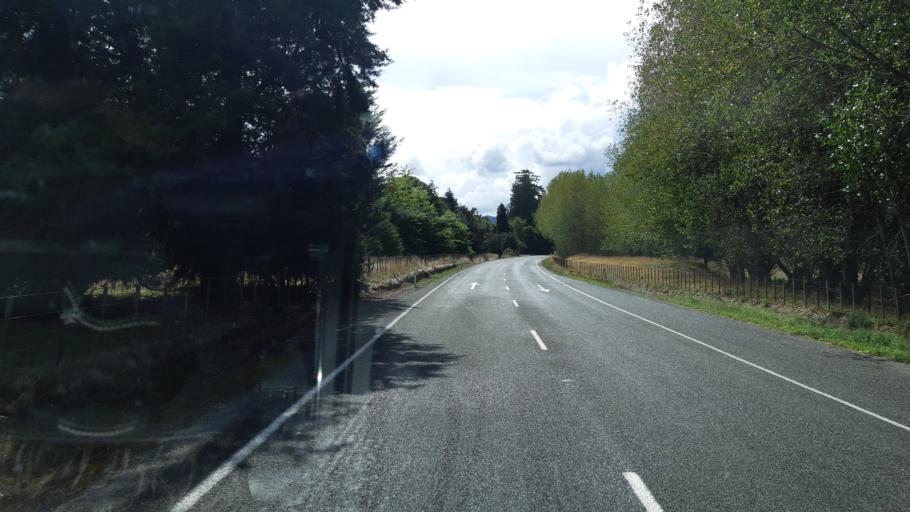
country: NZ
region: Tasman
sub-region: Tasman District
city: Wakefield
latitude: -41.4587
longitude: 172.8118
